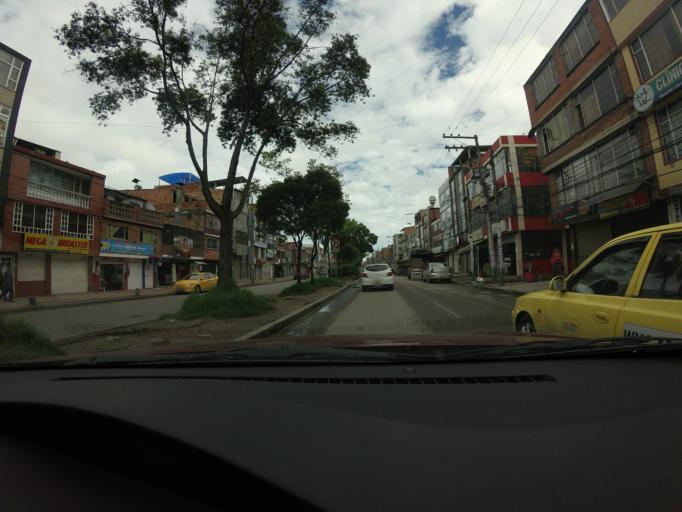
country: CO
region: Bogota D.C.
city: Bogota
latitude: 4.6036
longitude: -74.1511
